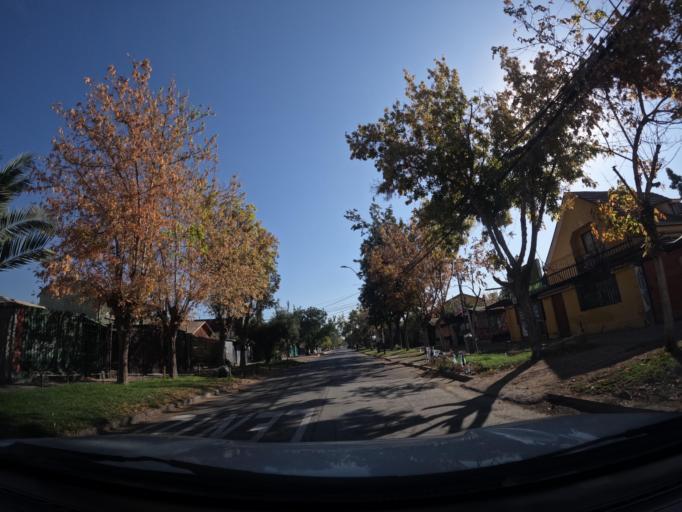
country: CL
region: Santiago Metropolitan
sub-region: Provincia de Santiago
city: Villa Presidente Frei, Nunoa, Santiago, Chile
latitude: -33.4682
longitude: -70.5697
